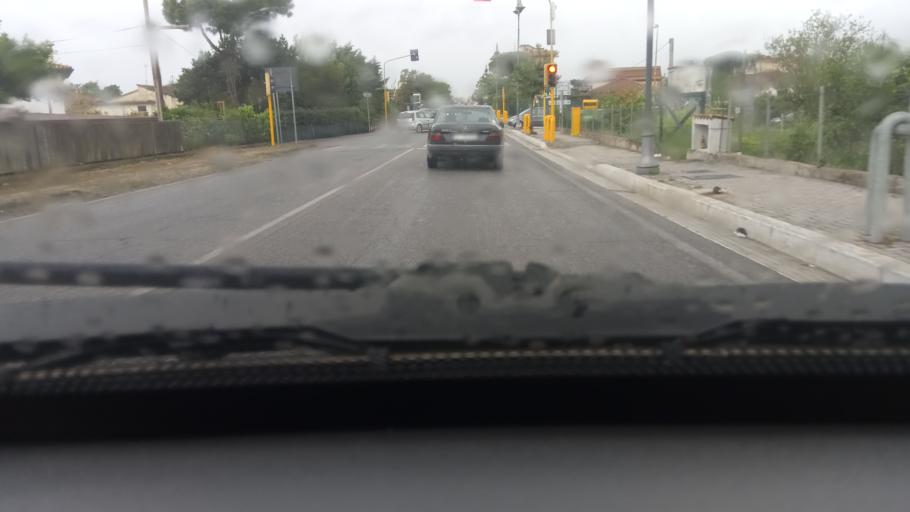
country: IT
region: Latium
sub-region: Provincia di Latina
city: Minturno
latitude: 41.2511
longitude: 13.7309
